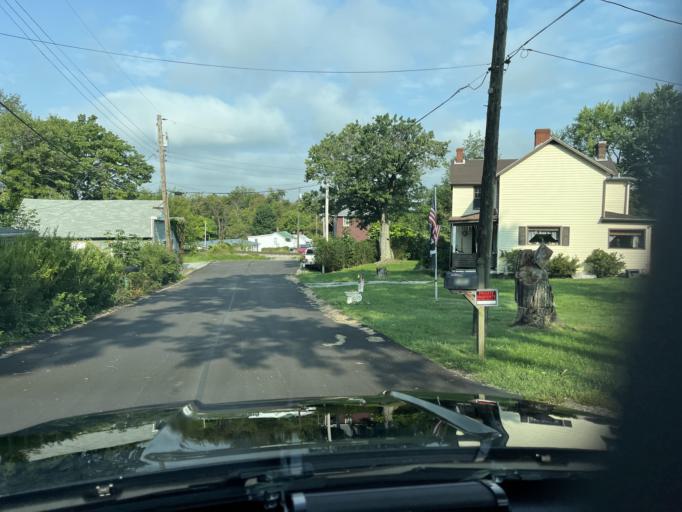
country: US
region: Pennsylvania
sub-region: Fayette County
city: Hopwood
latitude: 39.8604
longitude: -79.7136
